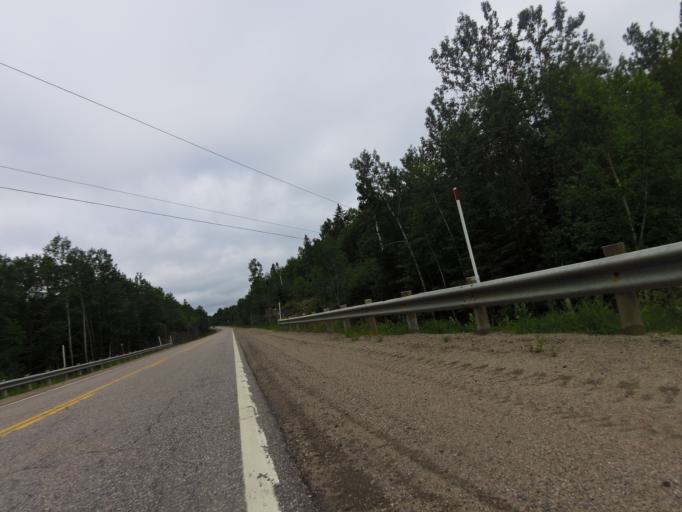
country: CA
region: Quebec
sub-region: Outaouais
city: Shawville
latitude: 45.9137
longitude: -76.3266
